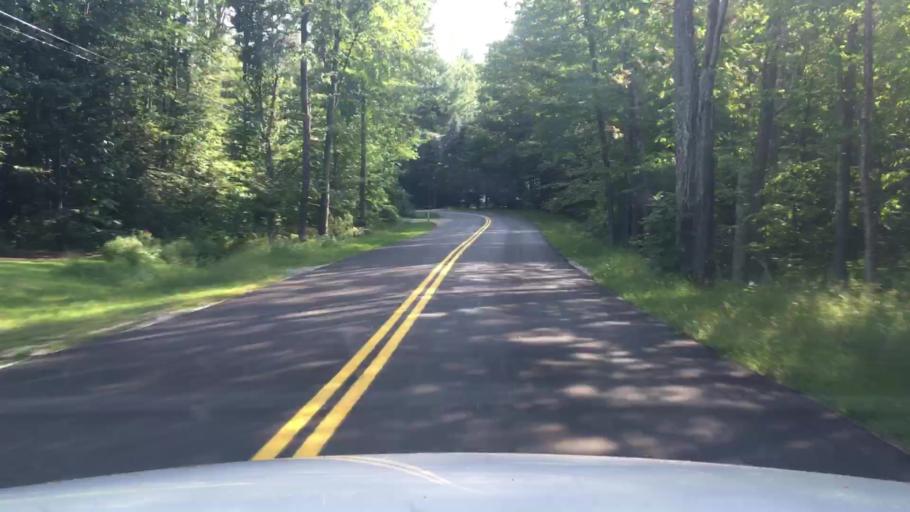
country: US
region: Maine
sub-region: Cumberland County
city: New Gloucester
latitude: 43.9422
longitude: -70.2875
